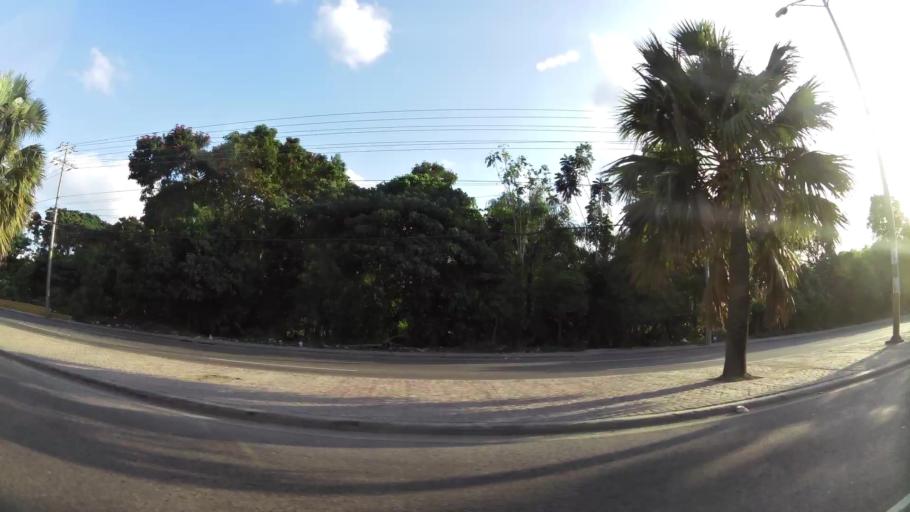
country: DO
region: Nacional
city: La Agustina
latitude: 18.5468
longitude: -69.9185
